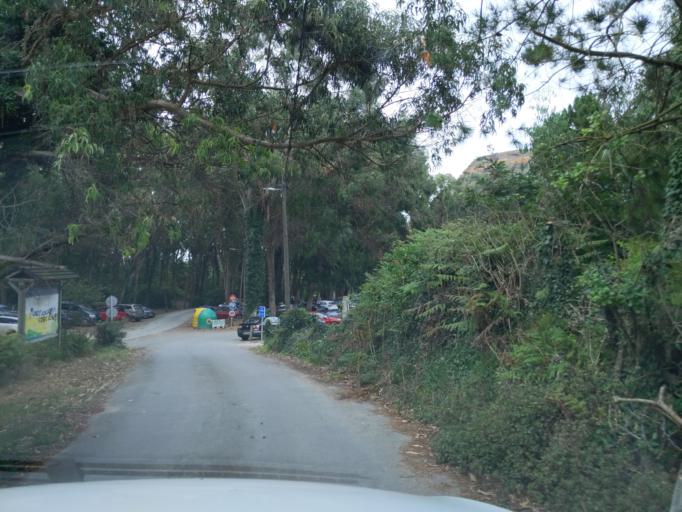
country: ES
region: Asturias
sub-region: Province of Asturias
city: Aviles
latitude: 43.6016
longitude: -5.9161
